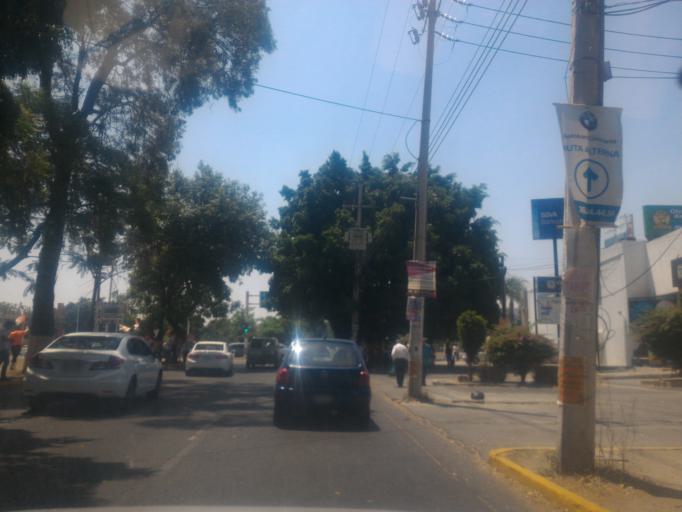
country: MX
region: Jalisco
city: Guadalajara
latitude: 20.6284
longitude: -103.4192
